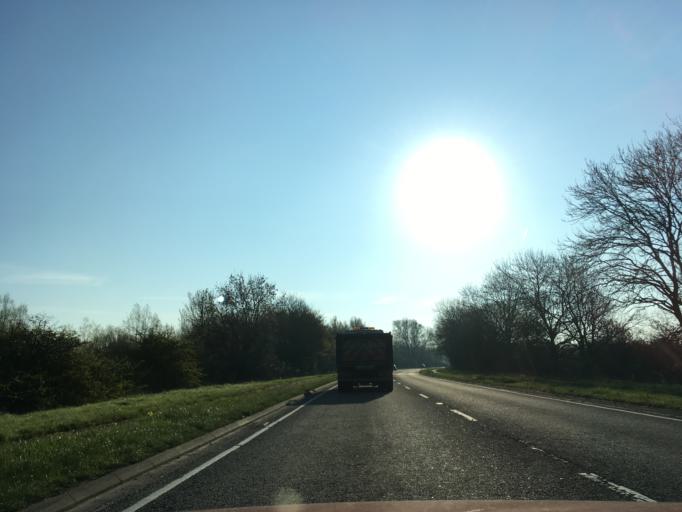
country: GB
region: England
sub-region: Oxfordshire
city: Yarnton
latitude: 51.7931
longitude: -1.3077
